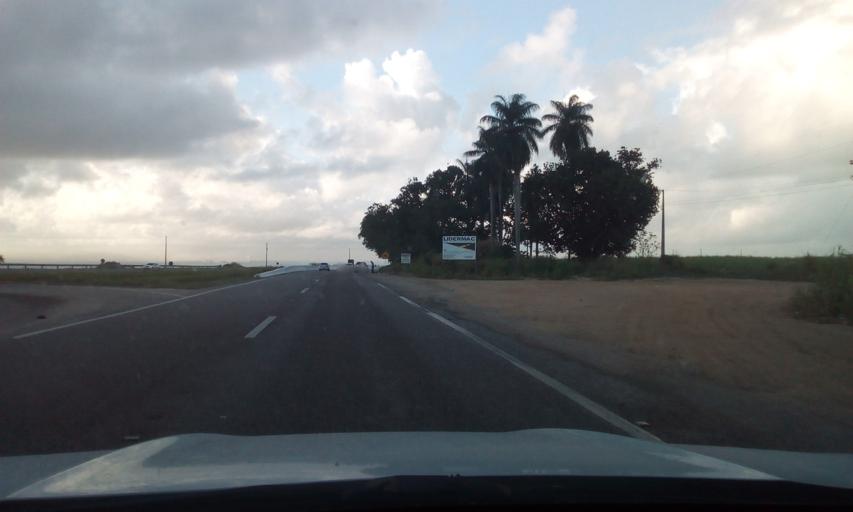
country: BR
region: Pernambuco
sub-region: Itapissuma
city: Itapissuma
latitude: -7.7335
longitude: -34.9417
